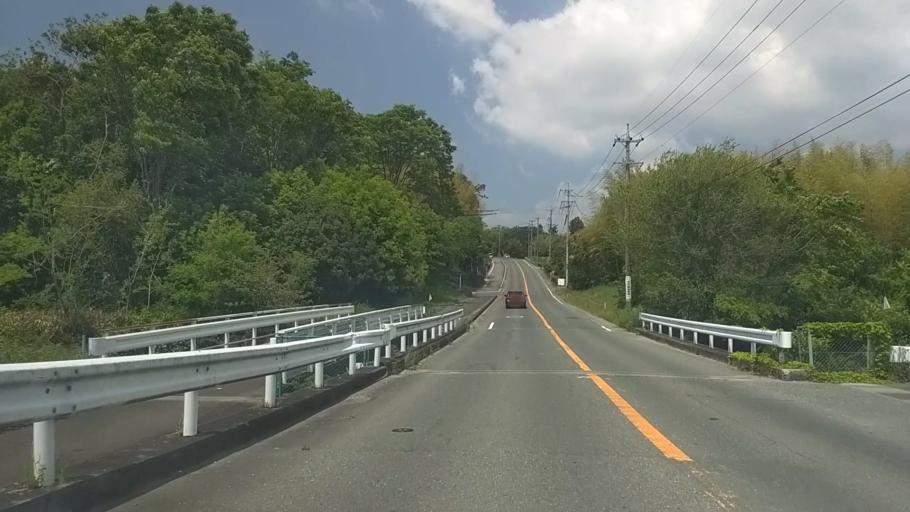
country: JP
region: Shizuoka
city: Hamamatsu
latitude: 34.7517
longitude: 137.6858
